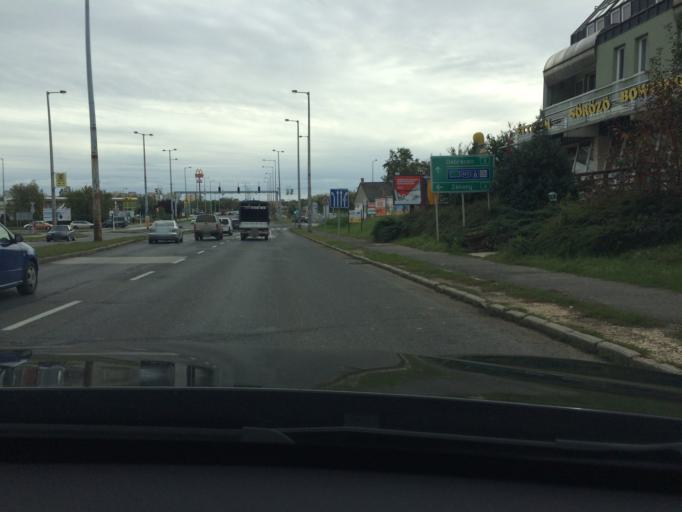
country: HU
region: Szabolcs-Szatmar-Bereg
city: Nyiregyhaza
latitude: 47.9636
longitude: 21.7233
